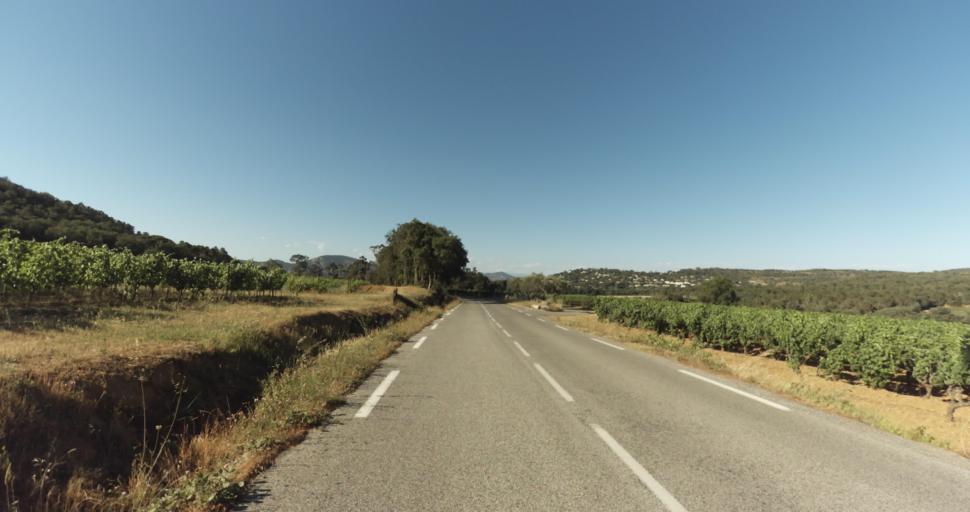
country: FR
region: Provence-Alpes-Cote d'Azur
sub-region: Departement du Var
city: Gassin
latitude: 43.2440
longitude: 6.5892
